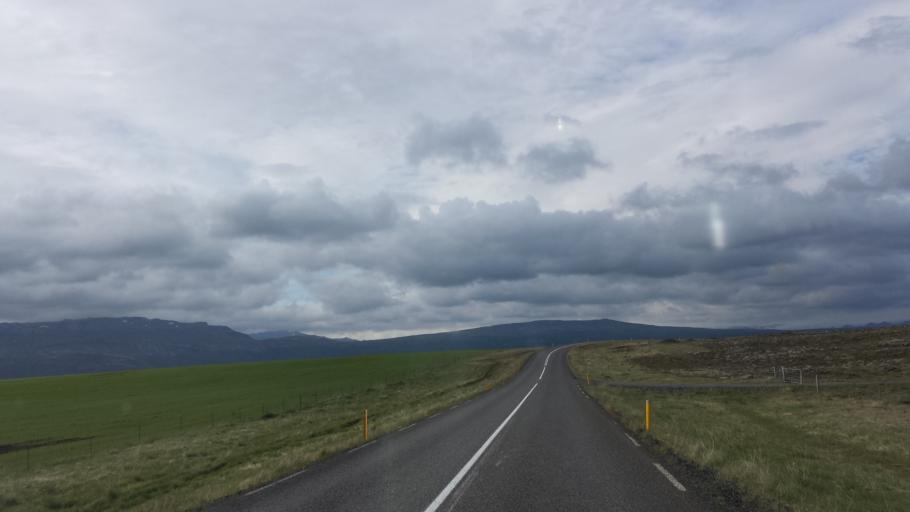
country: IS
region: South
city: Vestmannaeyjar
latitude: 64.2677
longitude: -20.2251
